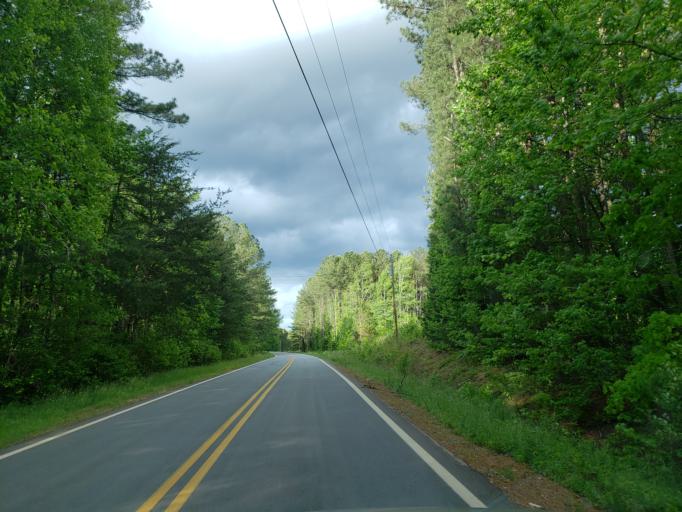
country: US
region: Georgia
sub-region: Haralson County
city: Tallapoosa
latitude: 33.8569
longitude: -85.3720
